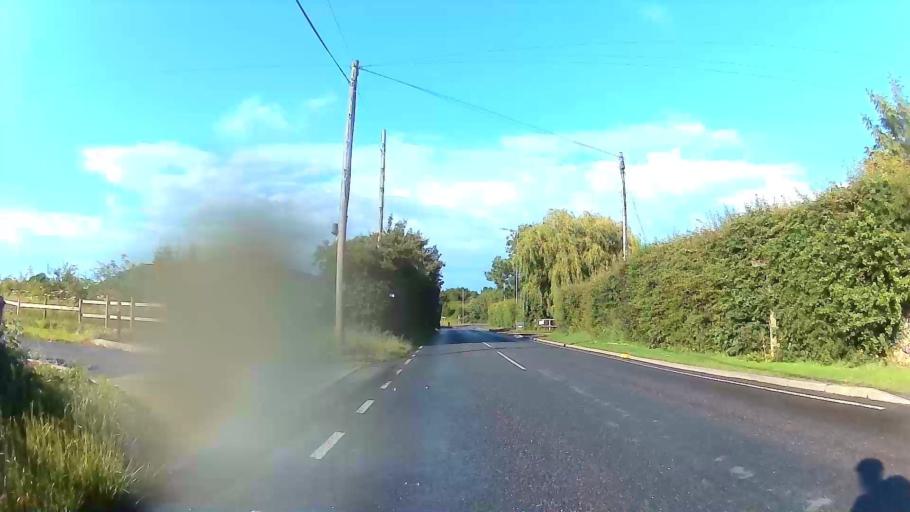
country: GB
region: England
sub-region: Essex
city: Writtle
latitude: 51.7246
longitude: 0.4077
